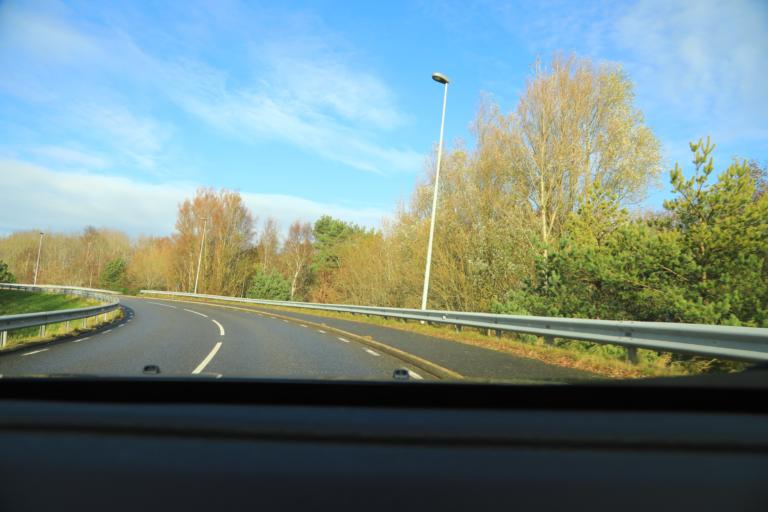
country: SE
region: Halland
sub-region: Varbergs Kommun
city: Varberg
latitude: 57.1695
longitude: 12.2323
